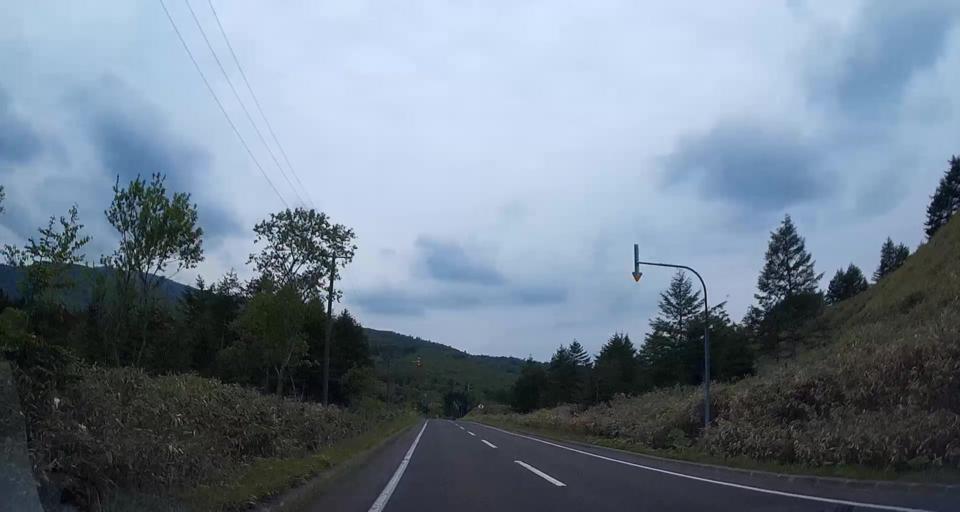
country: JP
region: Hokkaido
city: Shiraoi
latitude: 42.6732
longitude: 141.1650
